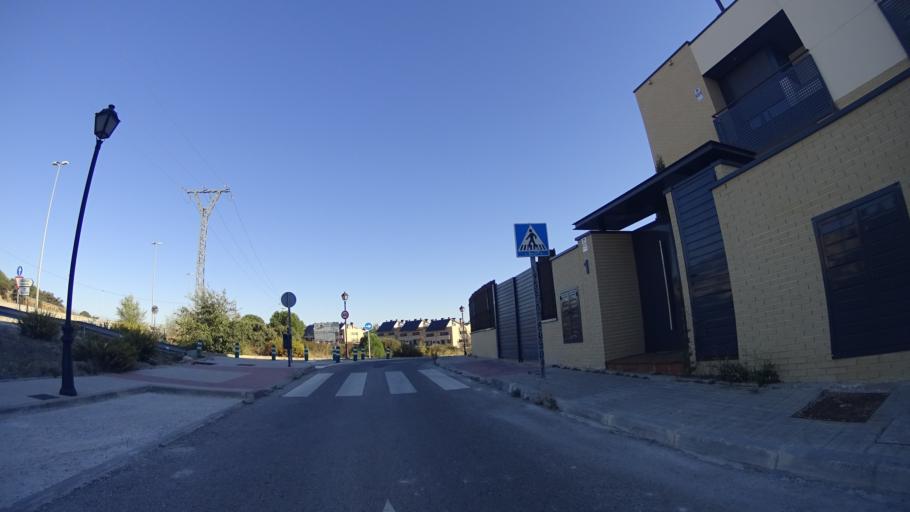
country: ES
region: Madrid
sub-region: Provincia de Madrid
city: Torrelodones
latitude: 40.5791
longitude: -3.9460
